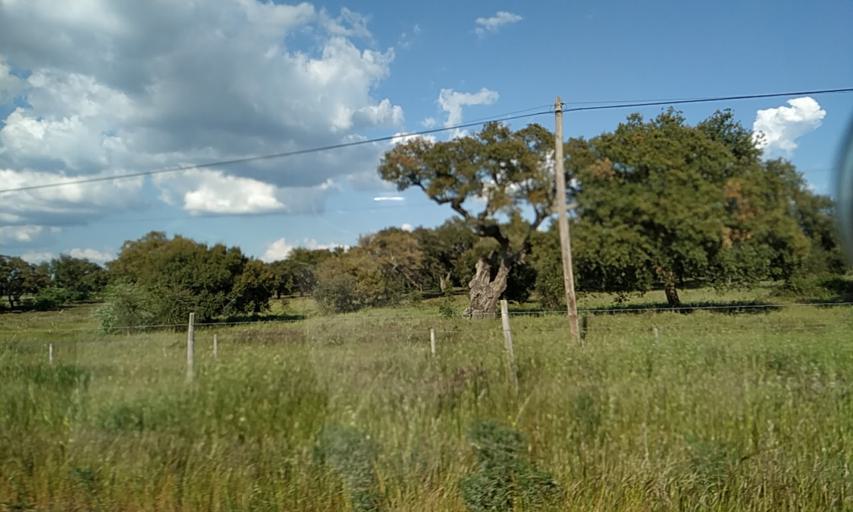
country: PT
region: Portalegre
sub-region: Portalegre
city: Urra
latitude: 39.1700
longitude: -7.4537
